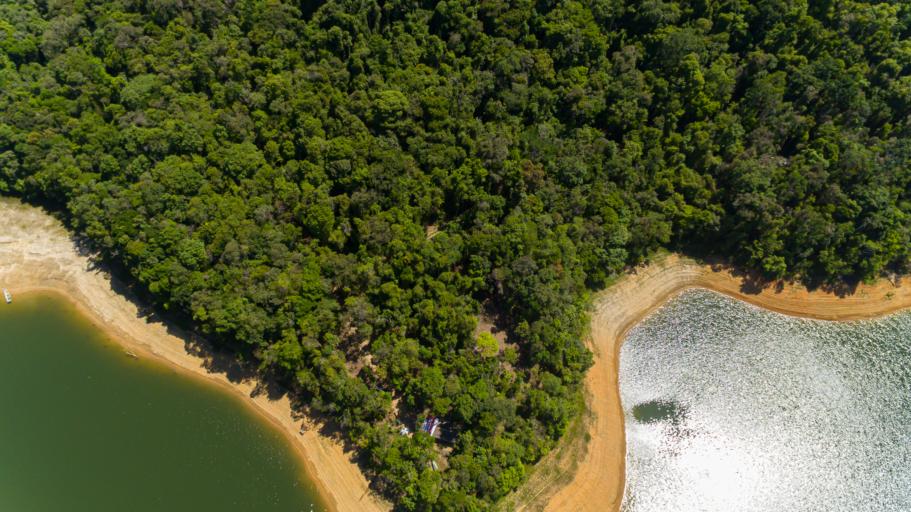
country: BR
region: Sao Paulo
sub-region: Juquitiba
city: Juquitiba
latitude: -24.0232
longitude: -47.2455
